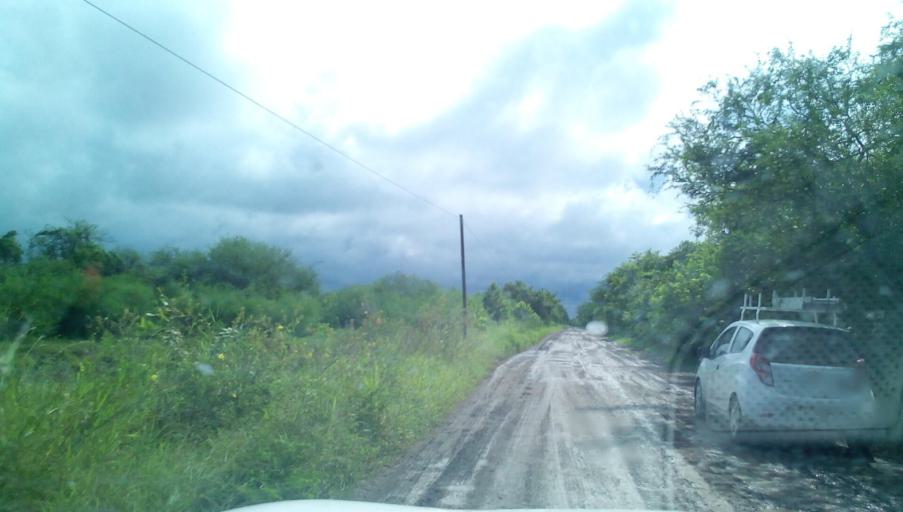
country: MX
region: Veracruz
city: Panuco
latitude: 21.8514
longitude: -98.1654
